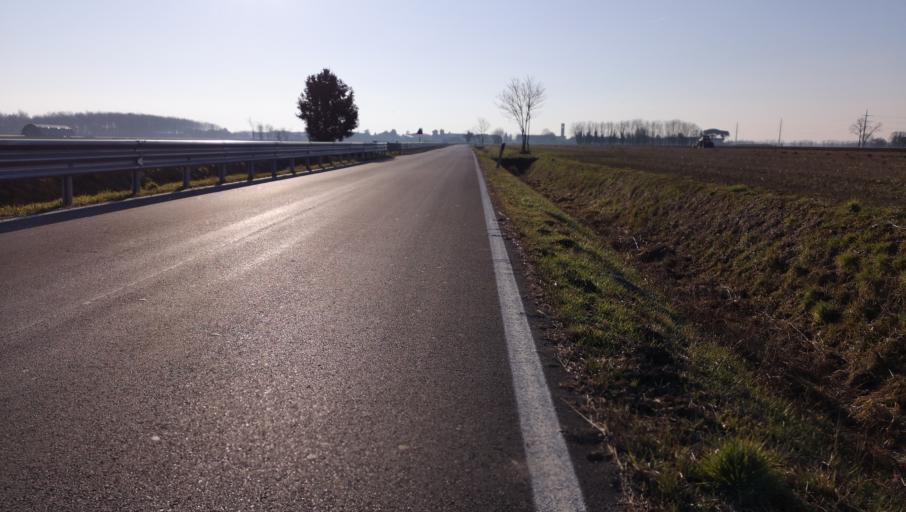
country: IT
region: Friuli Venezia Giulia
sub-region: Provincia di Udine
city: Percoto
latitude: 45.9568
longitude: 13.3061
